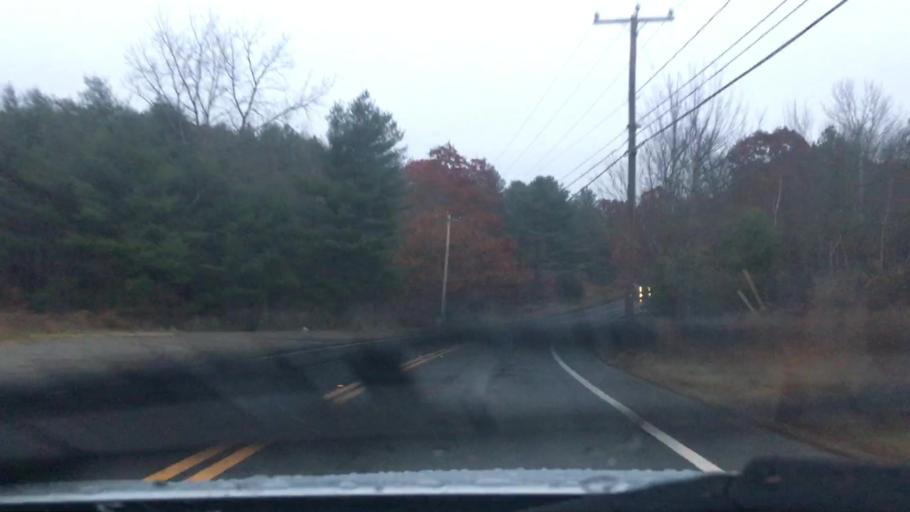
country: US
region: Massachusetts
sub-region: Hampden County
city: Southwick
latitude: 42.0628
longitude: -72.7108
